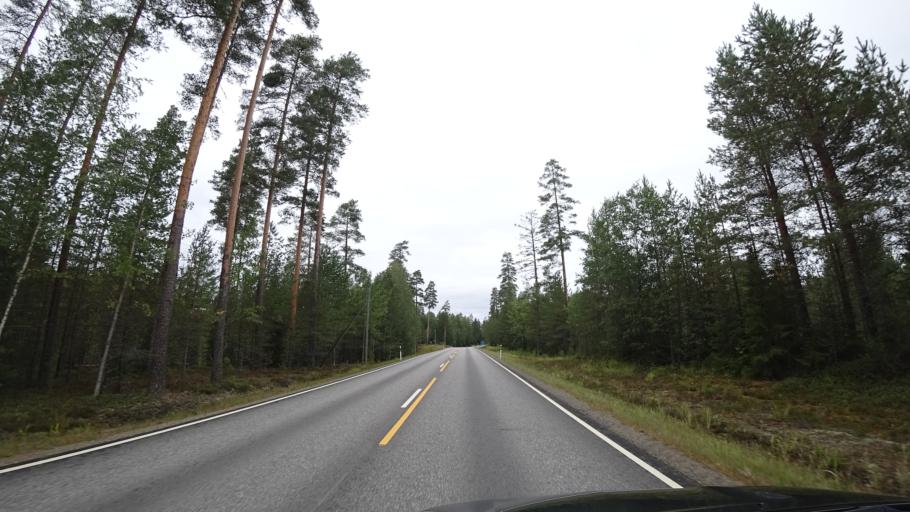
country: FI
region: Paijanne Tavastia
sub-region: Lahti
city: Auttoinen
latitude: 61.2102
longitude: 25.0878
